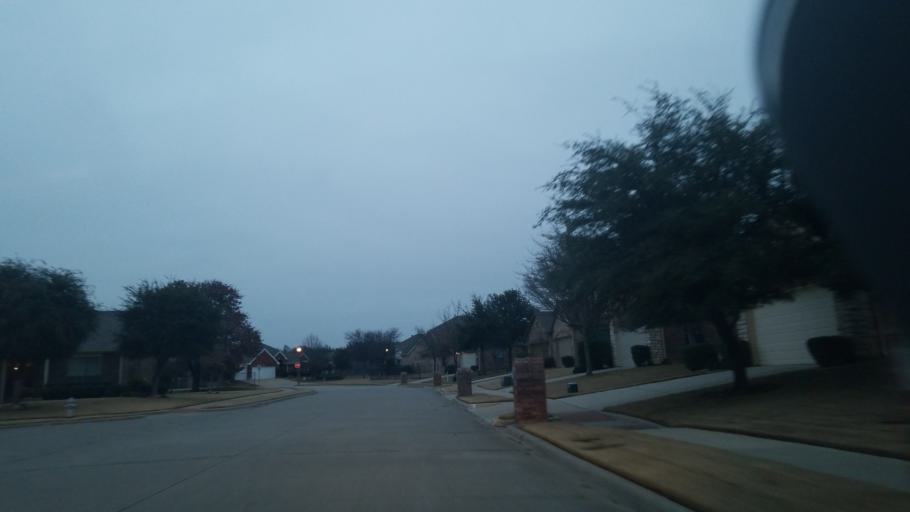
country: US
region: Texas
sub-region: Denton County
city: Corinth
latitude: 33.1506
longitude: -97.0916
